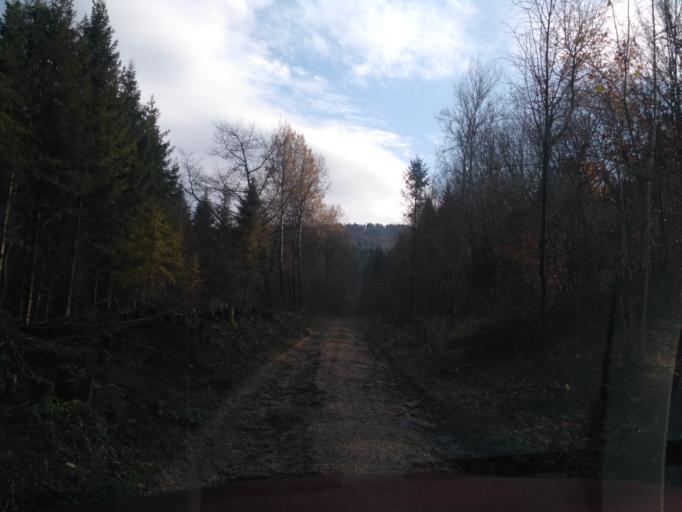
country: SK
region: Kosicky
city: Medzev
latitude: 48.7909
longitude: 20.7580
